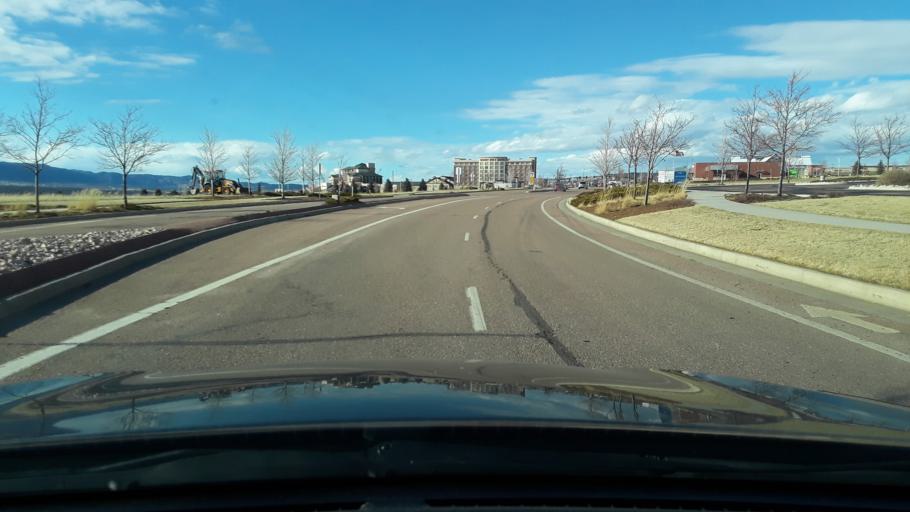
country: US
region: Colorado
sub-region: El Paso County
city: Air Force Academy
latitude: 38.9875
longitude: -104.8076
